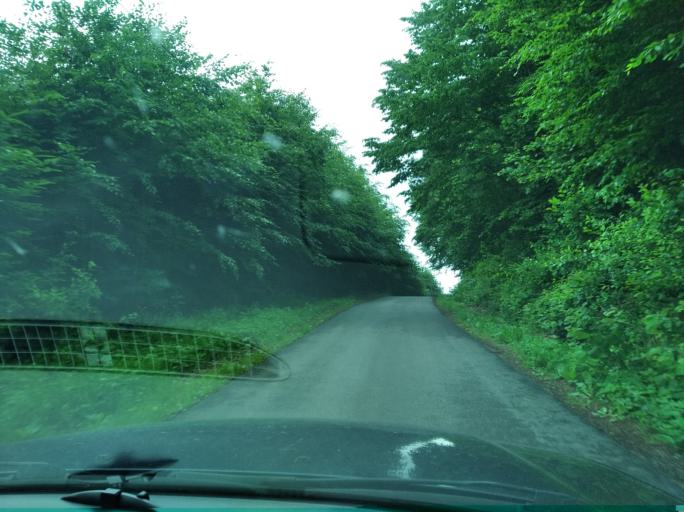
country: PL
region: Subcarpathian Voivodeship
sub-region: Powiat przemyski
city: Dubiecko
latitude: 49.8671
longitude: 22.4049
